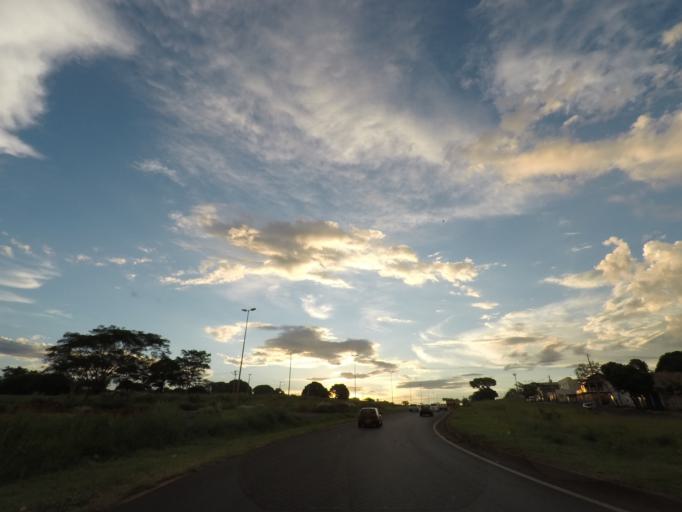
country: BR
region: Minas Gerais
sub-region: Uberaba
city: Uberaba
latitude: -19.7784
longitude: -47.9353
